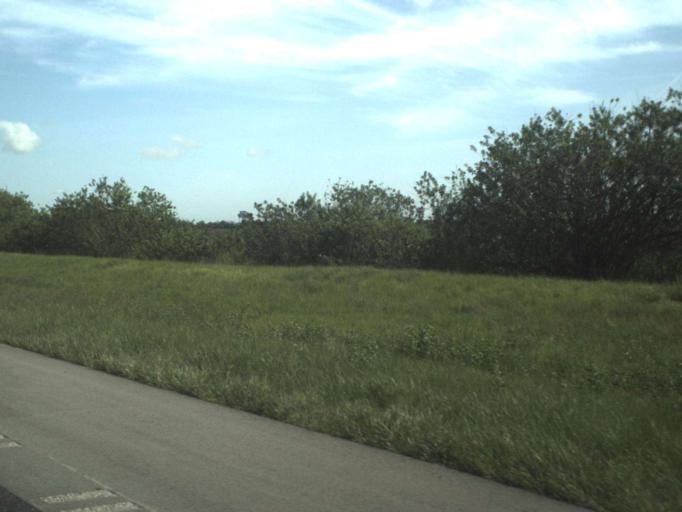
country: US
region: Florida
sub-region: Indian River County
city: West Vero Corridor
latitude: 27.6032
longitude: -80.5079
